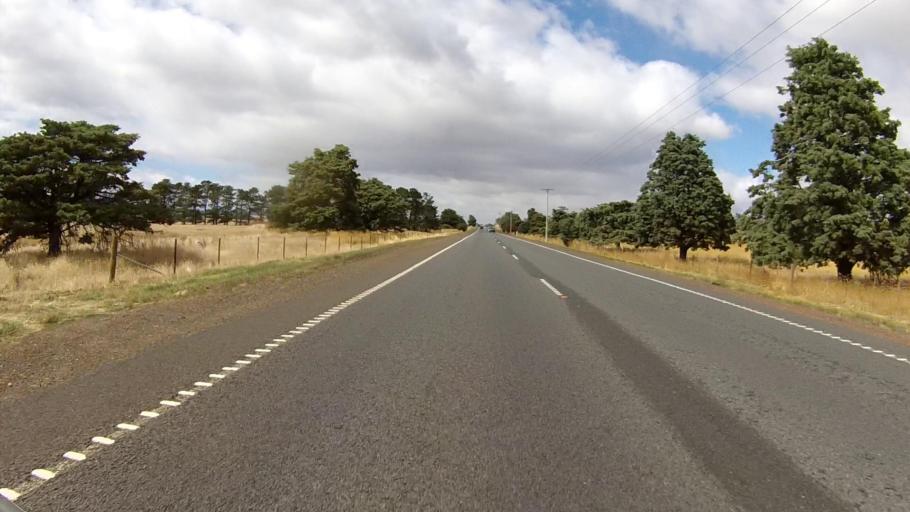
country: AU
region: Tasmania
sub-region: Northern Midlands
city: Evandale
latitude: -41.9494
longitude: 147.4944
